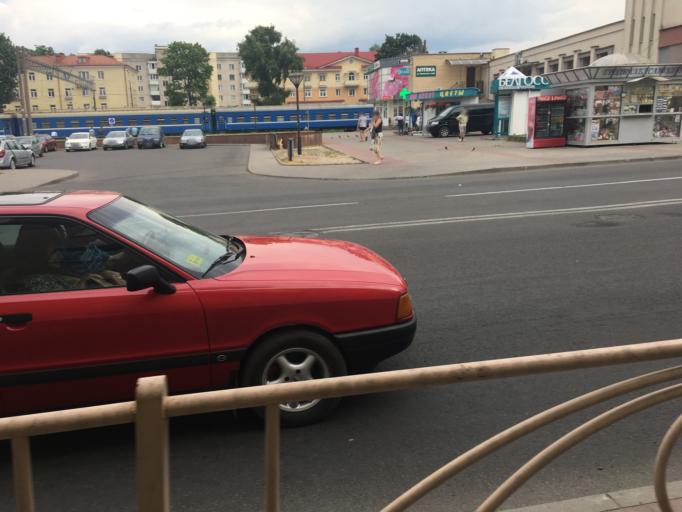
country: BY
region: Grodnenskaya
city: Hrodna
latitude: 53.6856
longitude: 23.8472
